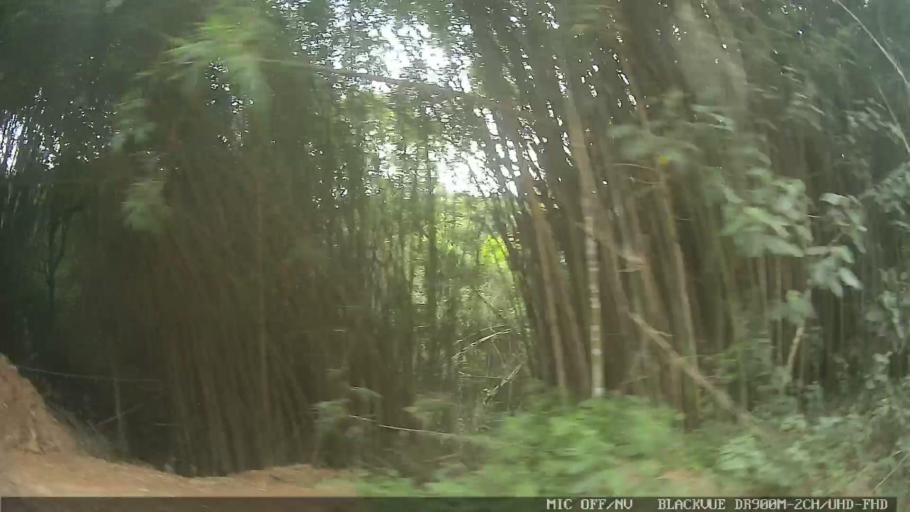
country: BR
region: Sao Paulo
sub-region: Bom Jesus Dos Perdoes
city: Bom Jesus dos Perdoes
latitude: -23.1424
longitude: -46.5111
